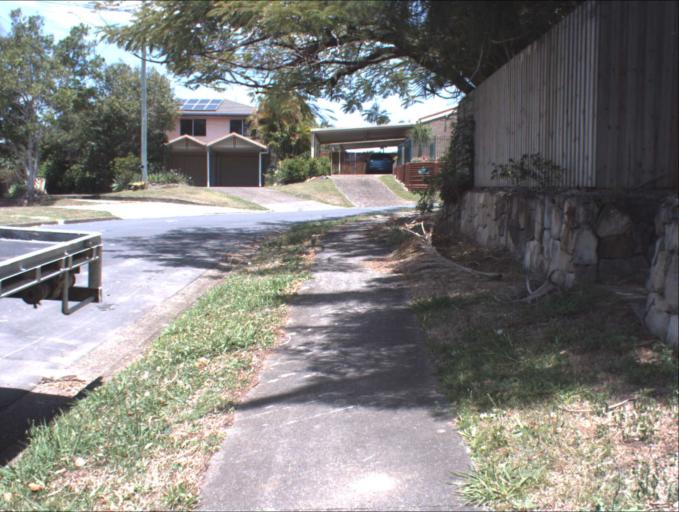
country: AU
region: Queensland
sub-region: Logan
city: Rochedale South
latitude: -27.5922
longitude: 153.1416
